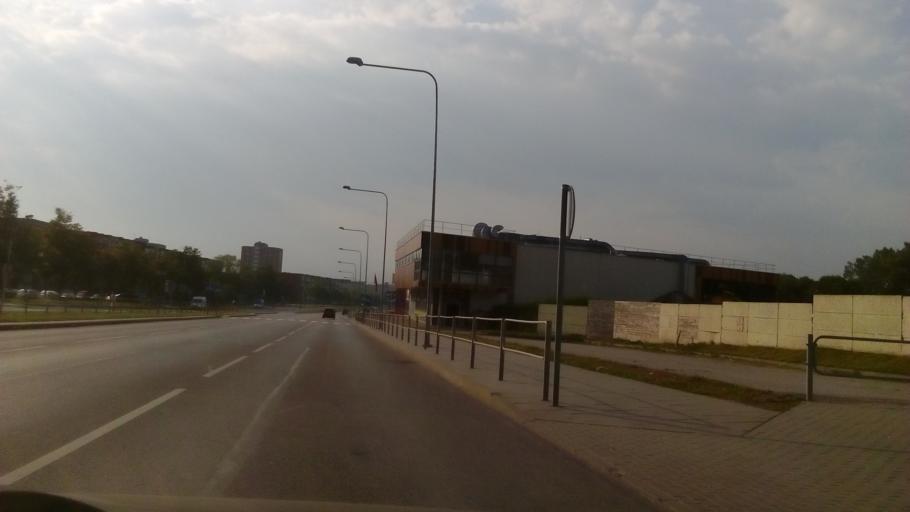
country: LT
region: Alytaus apskritis
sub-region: Alytus
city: Alytus
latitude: 54.4094
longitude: 24.0156
